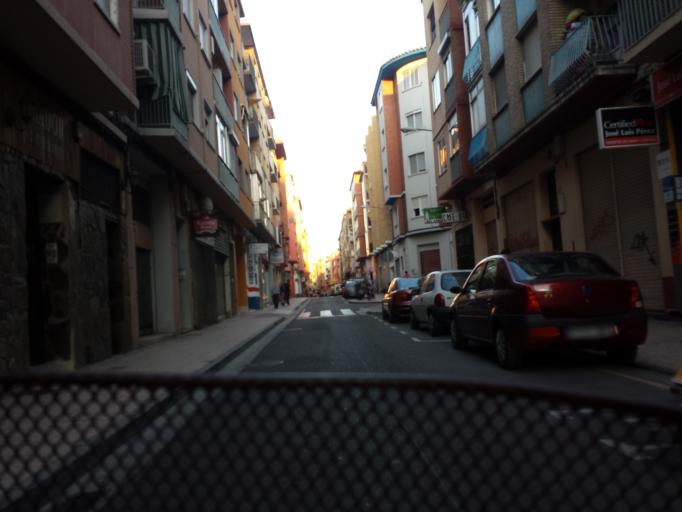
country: ES
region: Aragon
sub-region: Provincia de Zaragoza
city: Delicias
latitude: 41.6515
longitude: -0.9084
